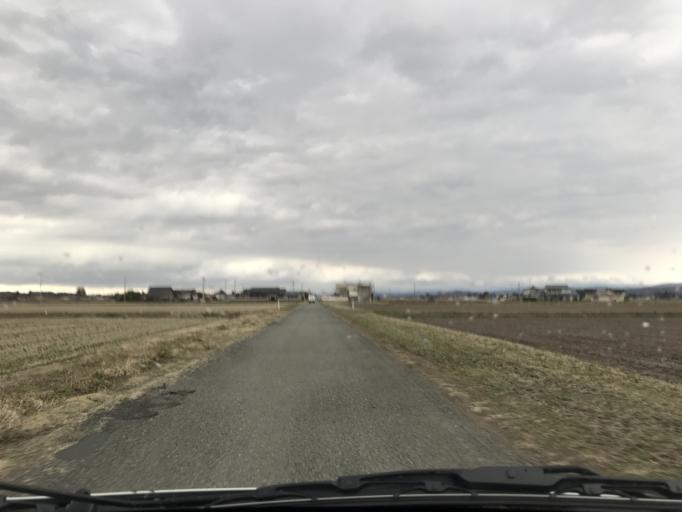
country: JP
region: Iwate
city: Mizusawa
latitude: 39.0792
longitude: 141.1565
